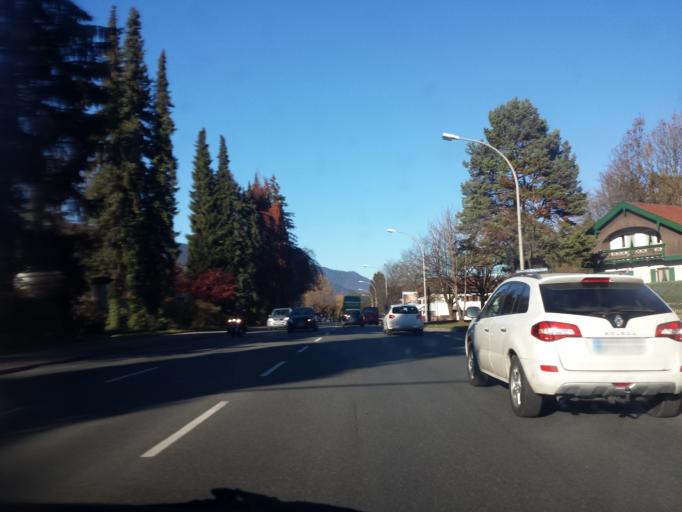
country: DE
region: Bavaria
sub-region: Upper Bavaria
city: Garmisch-Partenkirchen
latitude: 47.5034
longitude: 11.1029
